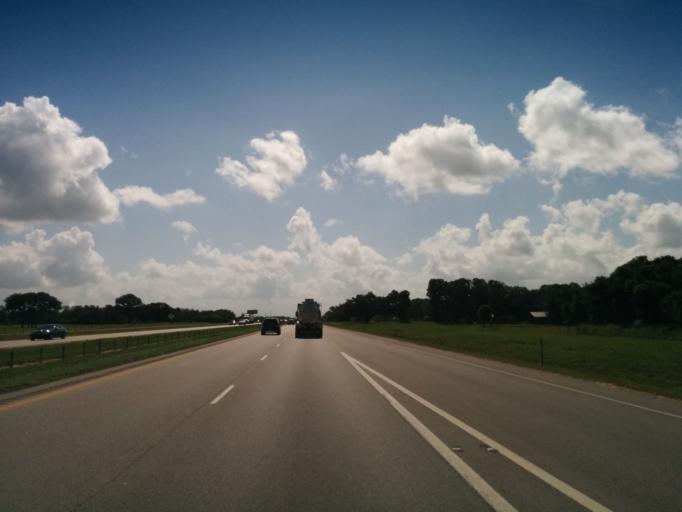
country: US
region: Texas
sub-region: Colorado County
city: Columbus
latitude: 29.6934
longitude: -96.5886
